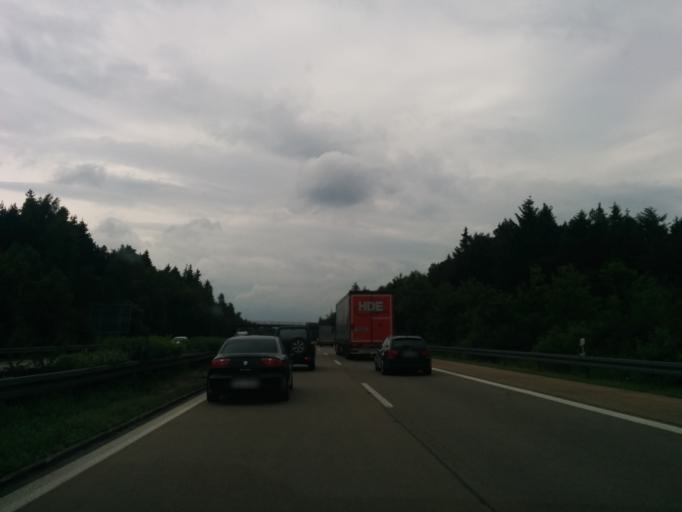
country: DE
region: Baden-Wuerttemberg
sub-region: Regierungsbezirk Stuttgart
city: Ellenberg
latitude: 49.0853
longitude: 10.2077
